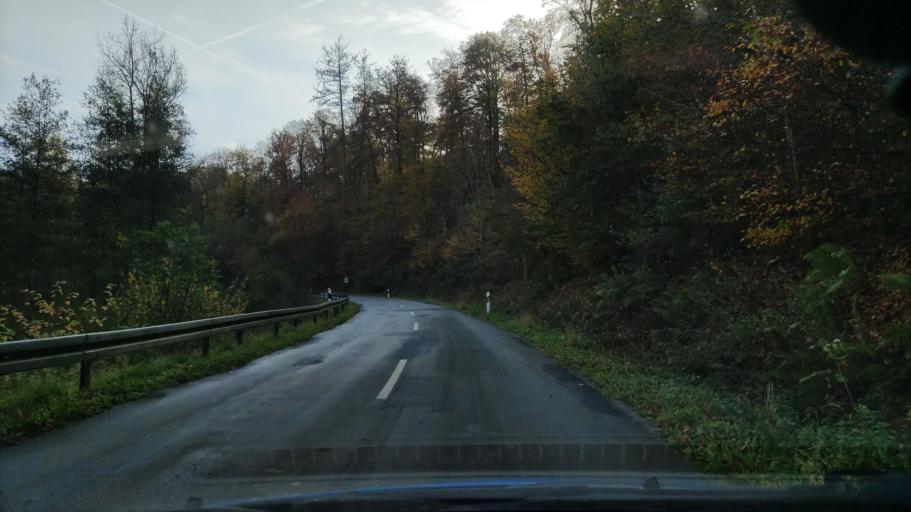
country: DE
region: Lower Saxony
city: Stadtoldendorf
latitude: 51.8865
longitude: 9.6045
